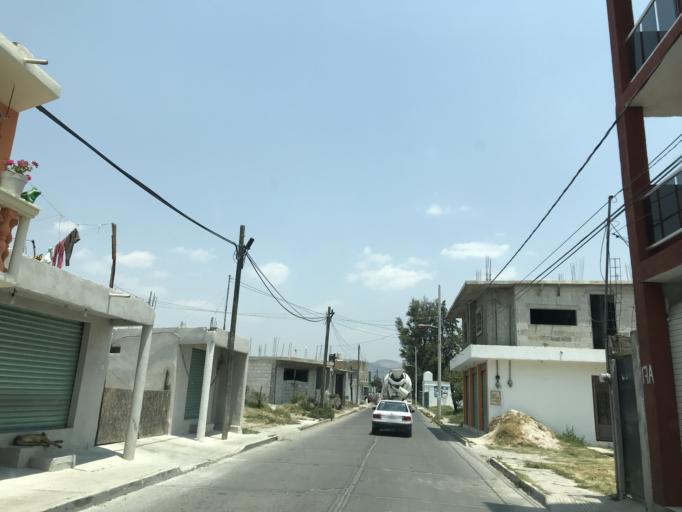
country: MX
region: Tlaxcala
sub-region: Ixtacuixtla de Mariano Matamoros
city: Villa Mariano Matamoros
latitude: 19.3130
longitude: -98.3725
